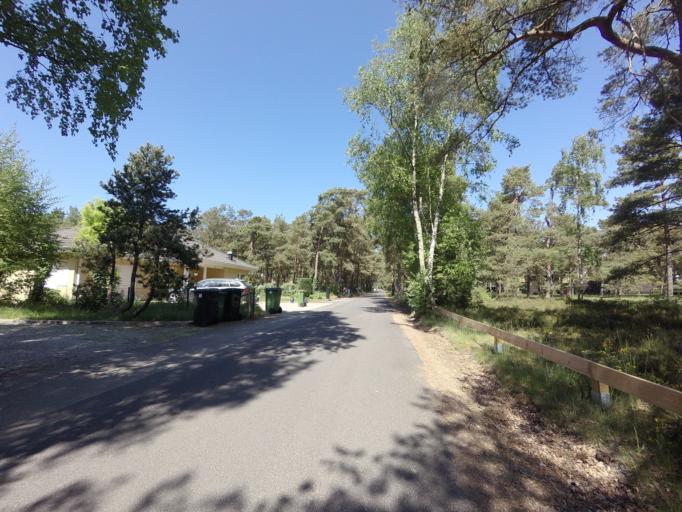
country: SE
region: Skane
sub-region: Vellinge Kommun
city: Hollviken
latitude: 55.4057
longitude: 12.9568
